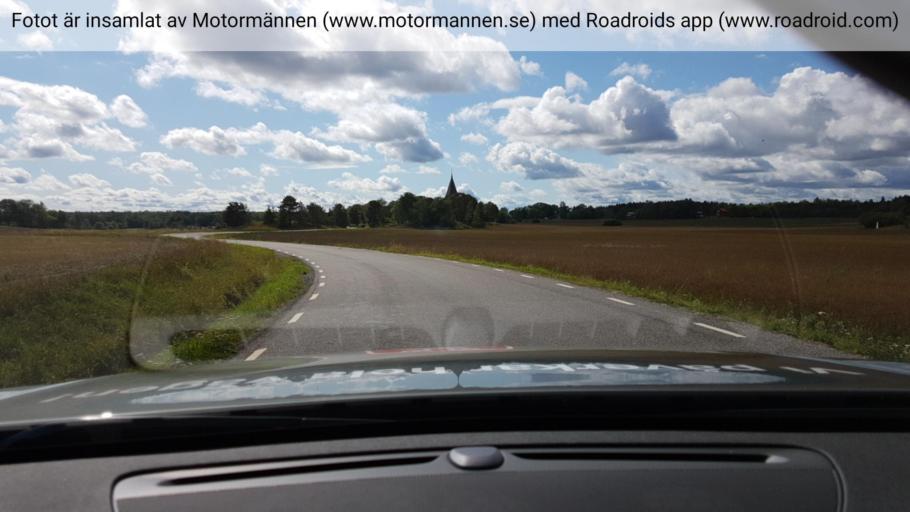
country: SE
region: Soedermanland
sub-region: Strangnas Kommun
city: Stallarholmen
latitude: 59.3816
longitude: 17.2602
